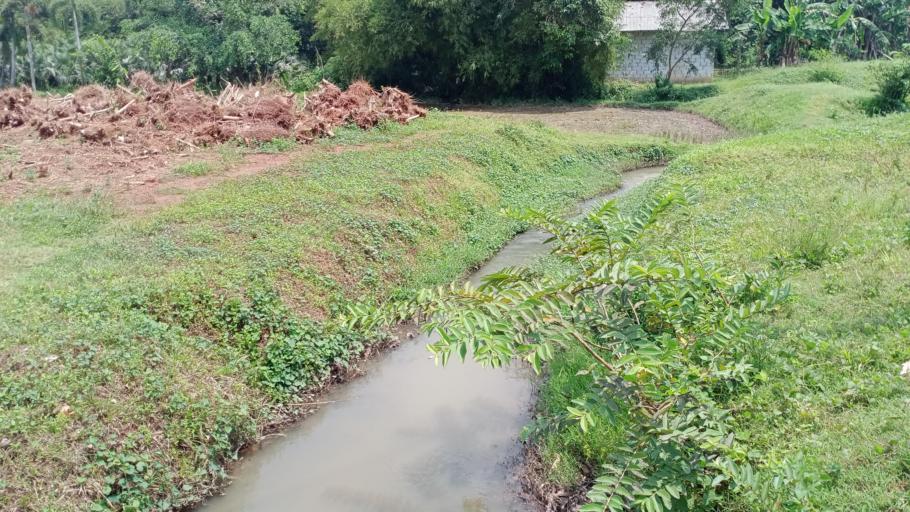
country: ID
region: West Java
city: Cileungsir
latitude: -6.3909
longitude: 107.0748
